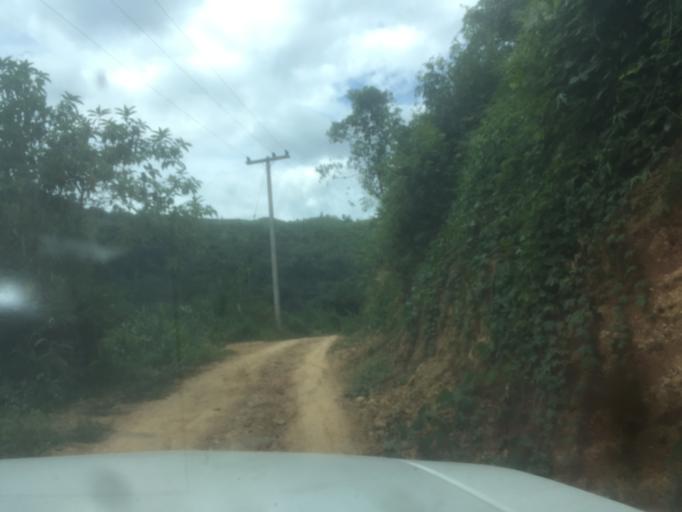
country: LA
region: Phongsali
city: Khoa
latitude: 20.9111
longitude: 102.5599
